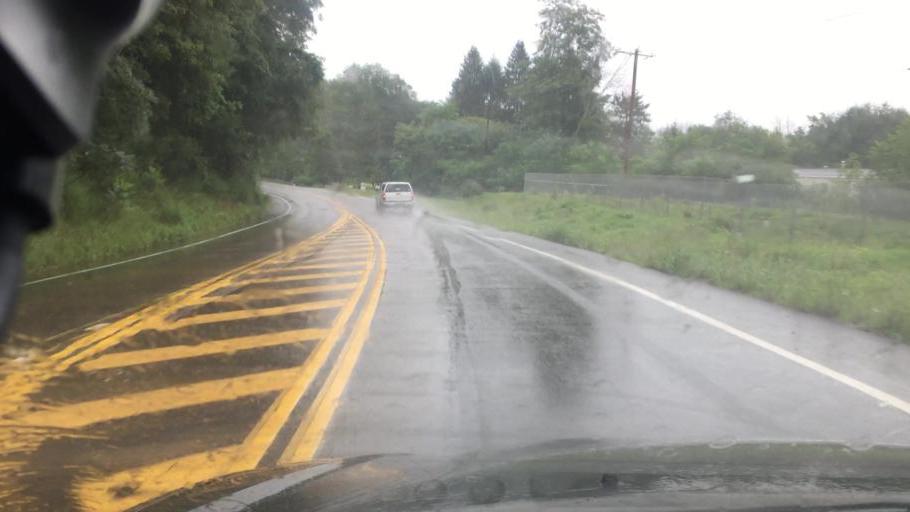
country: US
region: Pennsylvania
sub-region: Luzerne County
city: White Haven
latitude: 41.0490
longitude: -75.7770
